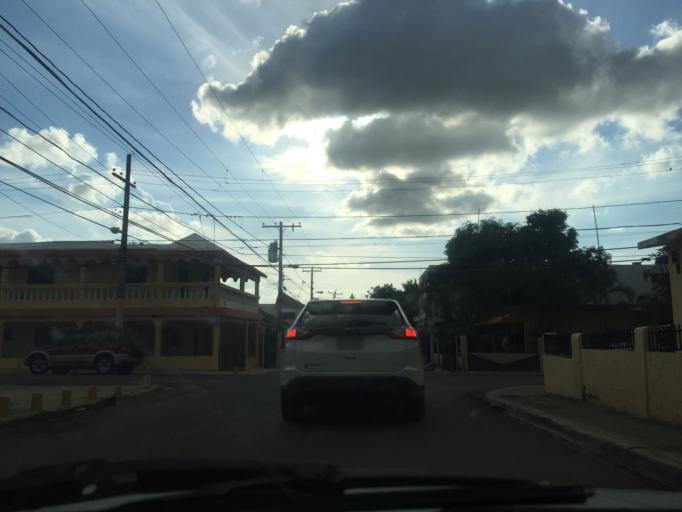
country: DO
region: Santiago
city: Santiago de los Caballeros
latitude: 19.4371
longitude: -70.6706
